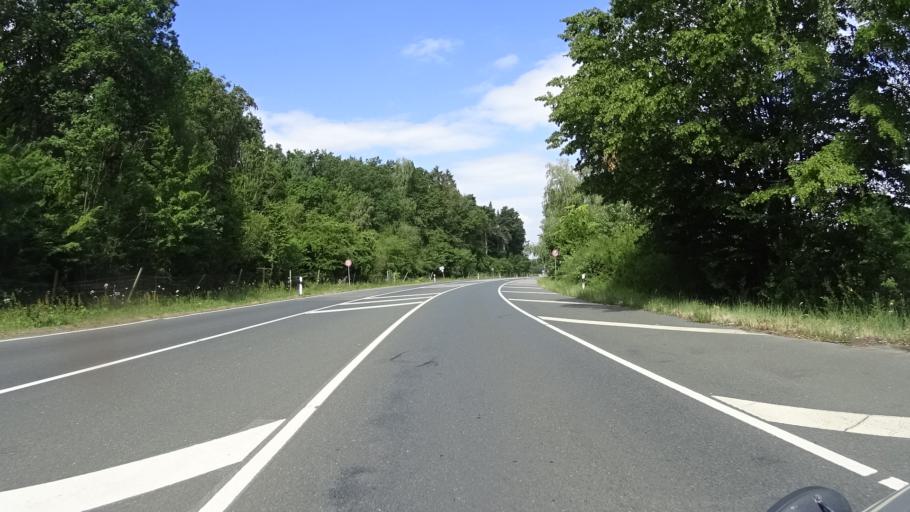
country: DE
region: Lower Saxony
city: Goslar
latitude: 51.9182
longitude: 10.4054
